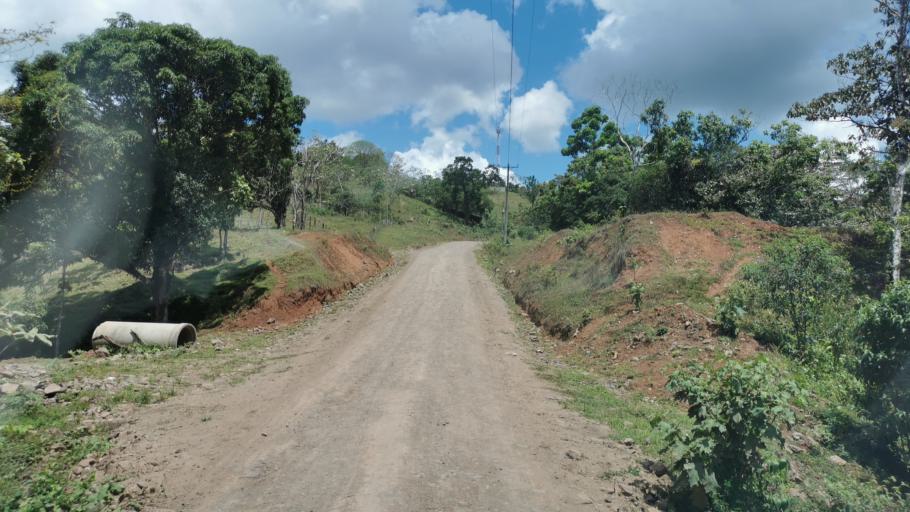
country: NI
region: Atlantico Sur
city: Rama
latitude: 12.3542
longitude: -84.2538
